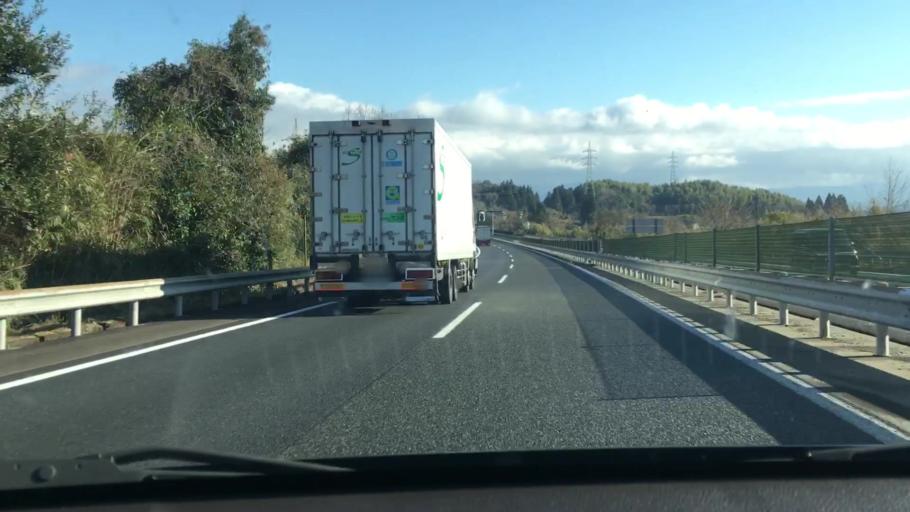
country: JP
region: Kumamoto
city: Hitoyoshi
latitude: 32.2371
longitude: 130.7627
